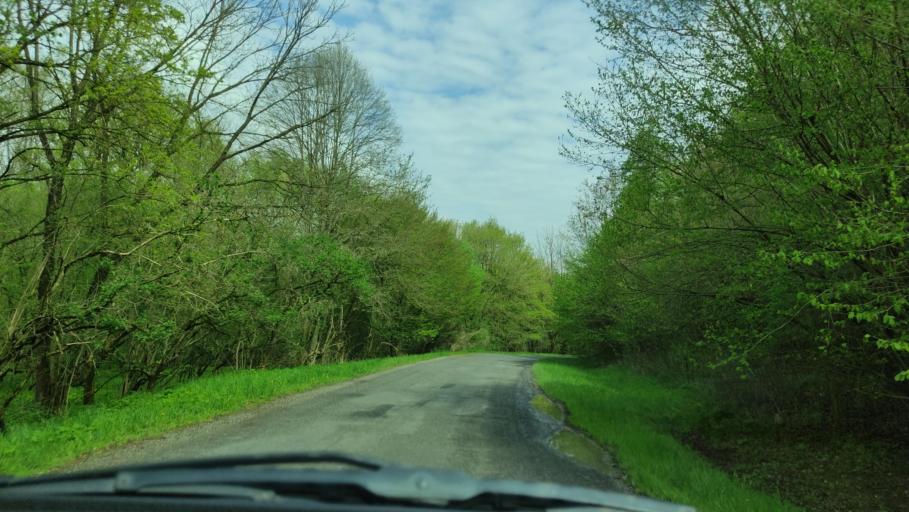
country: HU
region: Baranya
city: Komlo
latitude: 46.2568
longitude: 18.2124
